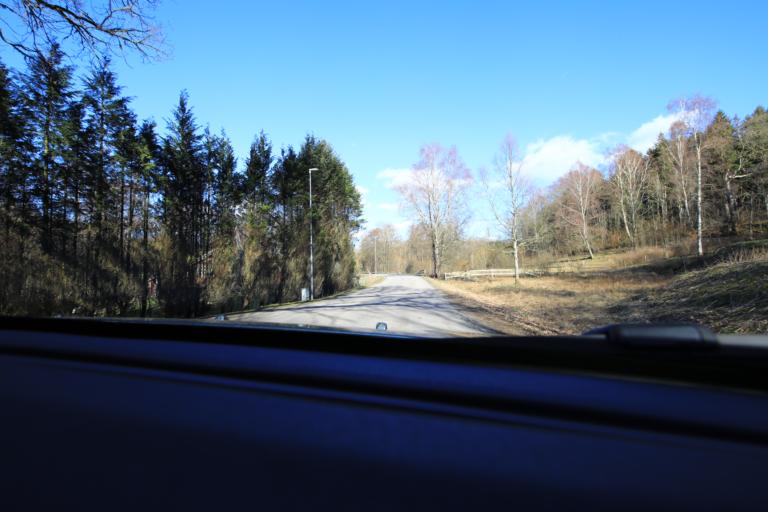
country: SE
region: Halland
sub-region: Varbergs Kommun
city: Tvaaker
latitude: 57.0643
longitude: 12.4850
